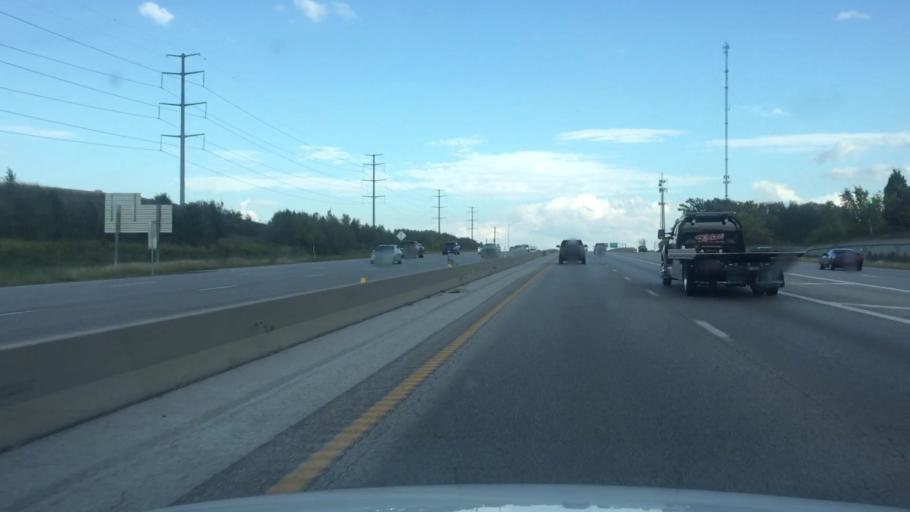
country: US
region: Missouri
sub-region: Jackson County
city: Lees Summit
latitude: 38.9346
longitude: -94.4249
